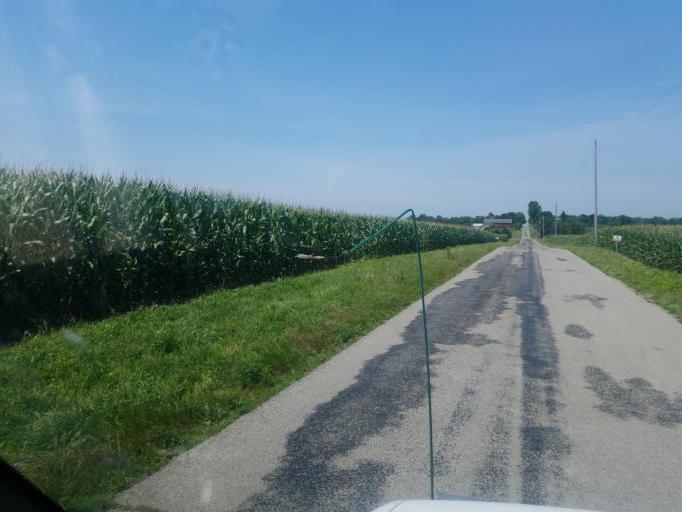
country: US
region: Ohio
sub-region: Logan County
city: West Liberty
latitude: 40.2892
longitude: -83.7794
